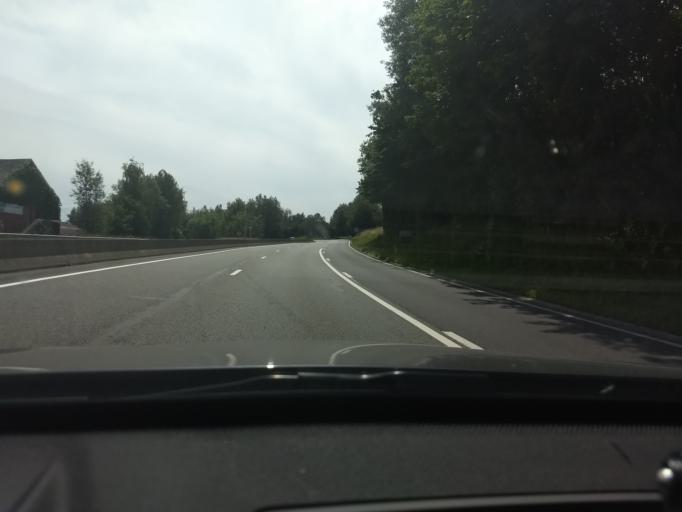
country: BE
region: Wallonia
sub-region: Province du Brabant Wallon
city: Louvain-la-Neuve
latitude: 50.6633
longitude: 4.6036
